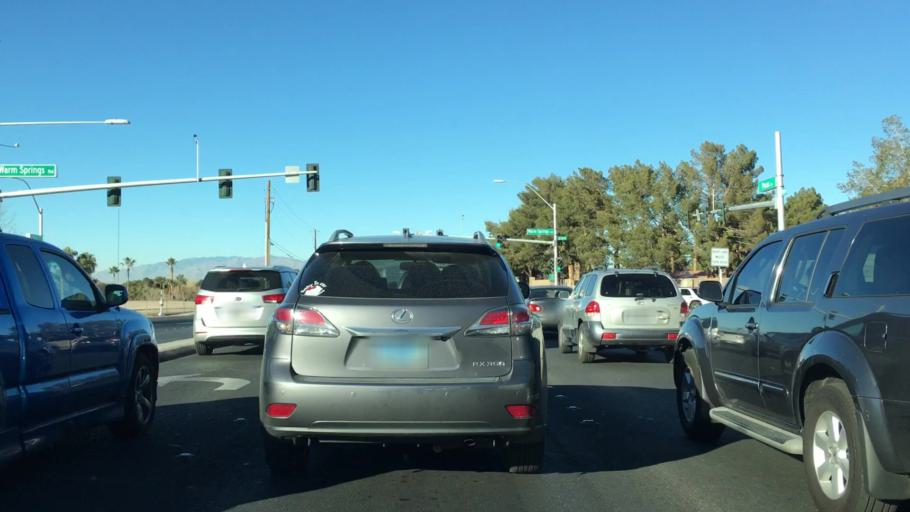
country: US
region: Nevada
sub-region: Clark County
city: Whitney
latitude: 36.0567
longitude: -115.1003
